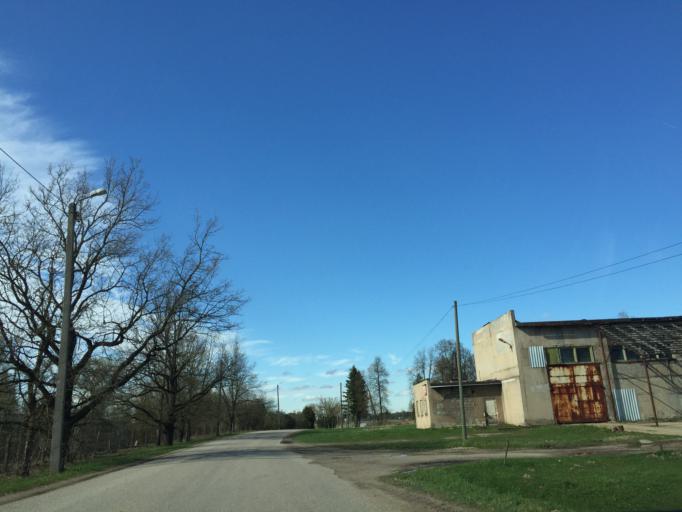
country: EE
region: Valgamaa
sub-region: Valga linn
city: Valga
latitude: 57.8664
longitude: 26.2514
